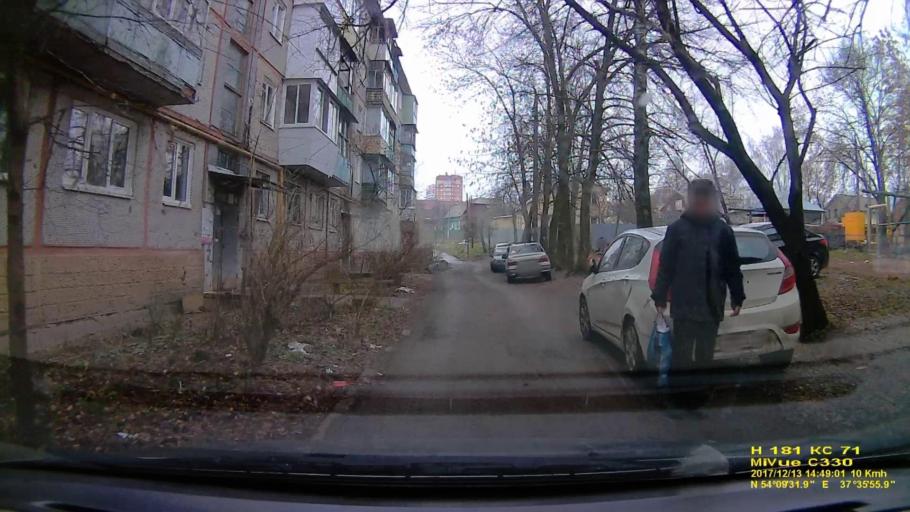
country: RU
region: Tula
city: Mendeleyevskiy
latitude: 54.1588
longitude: 37.5989
